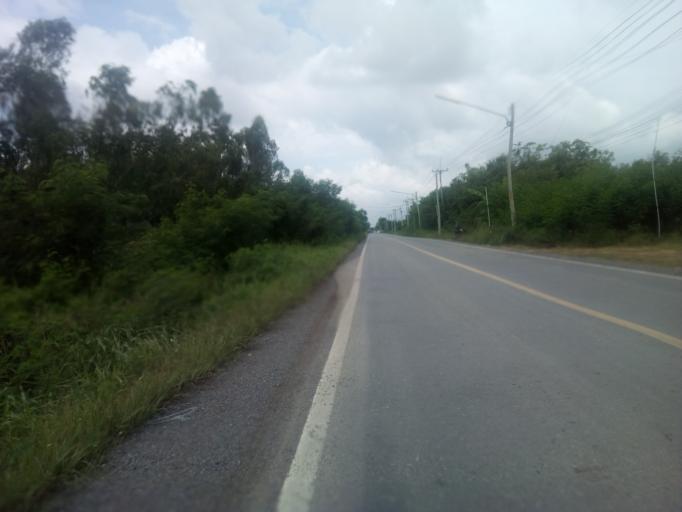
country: TH
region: Pathum Thani
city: Ban Lam Luk Ka
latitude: 13.9939
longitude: 100.8215
